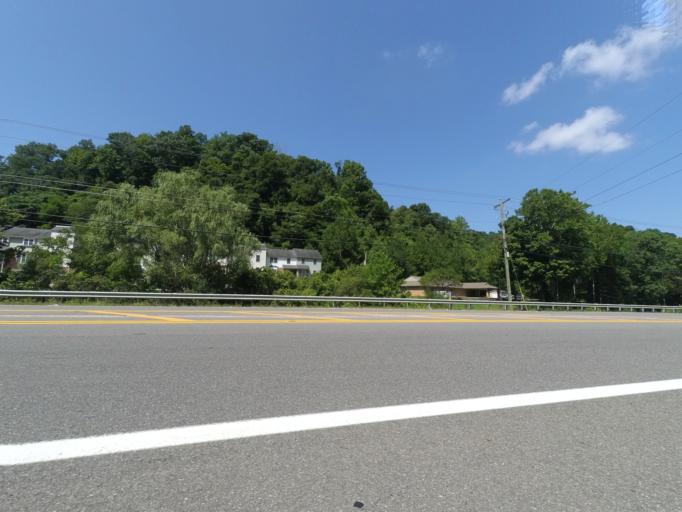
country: US
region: West Virginia
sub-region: Cabell County
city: Huntington
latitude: 38.3842
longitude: -82.4570
